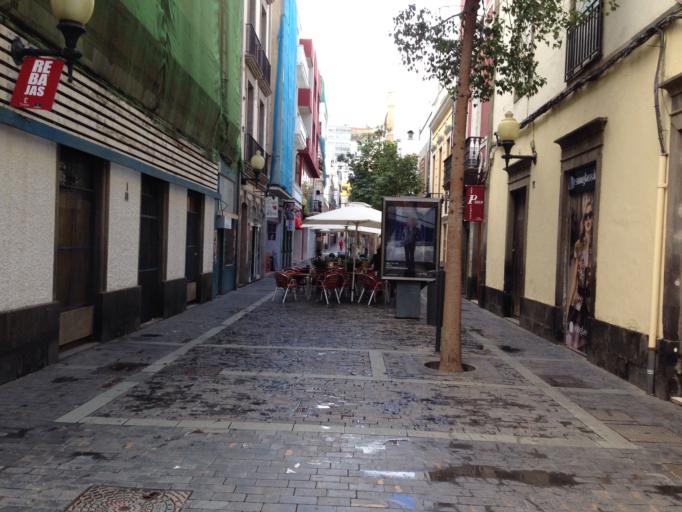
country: ES
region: Canary Islands
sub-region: Provincia de Las Palmas
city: Las Palmas de Gran Canaria
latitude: 28.1052
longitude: -15.4159
